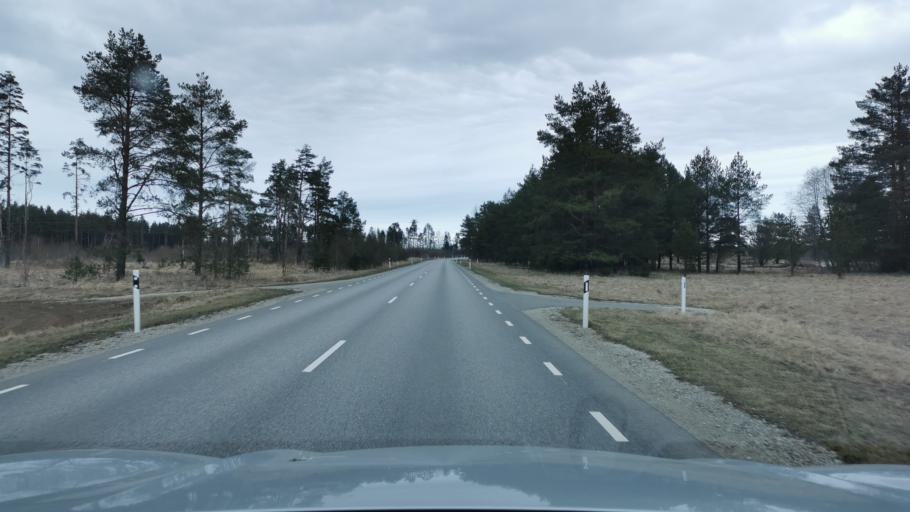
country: EE
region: Ida-Virumaa
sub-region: Puessi linn
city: Pussi
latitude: 59.3591
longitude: 27.0244
